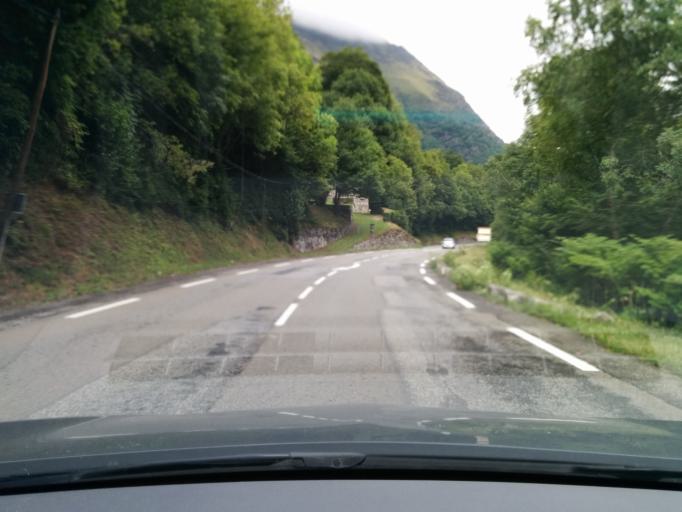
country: FR
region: Midi-Pyrenees
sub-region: Departement des Hautes-Pyrenees
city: Saint-Lary-Soulan
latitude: 42.7929
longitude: 0.2646
